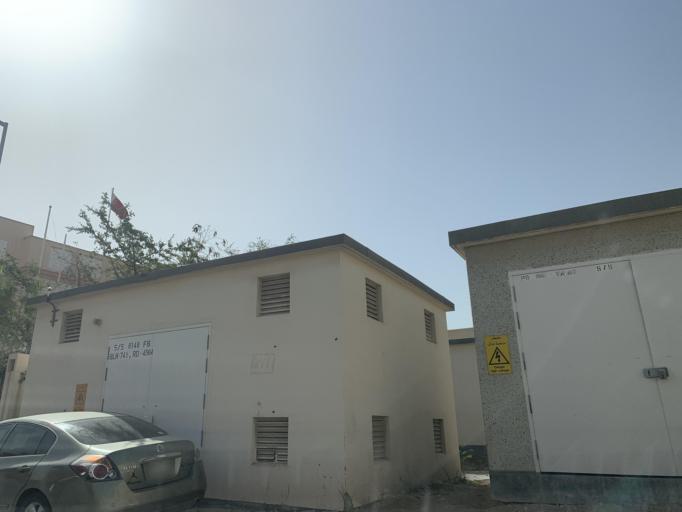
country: BH
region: Northern
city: Ar Rifa'
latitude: 26.1454
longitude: 50.5816
